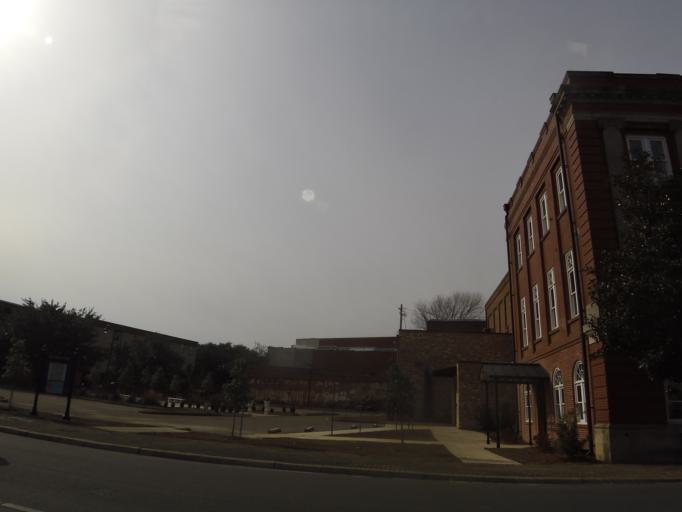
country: US
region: Alabama
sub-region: Houston County
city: Dothan
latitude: 31.2240
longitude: -85.3910
